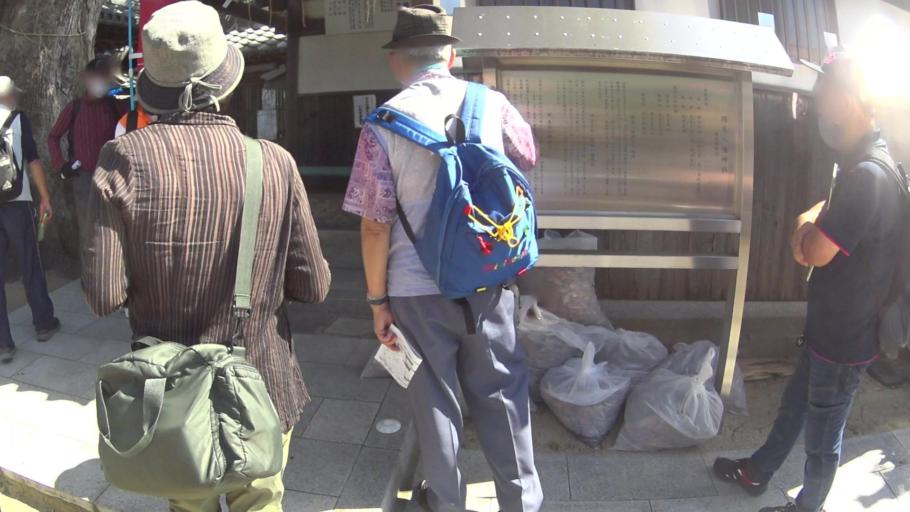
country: JP
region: Osaka
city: Matsubara
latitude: 34.5293
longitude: 135.5015
